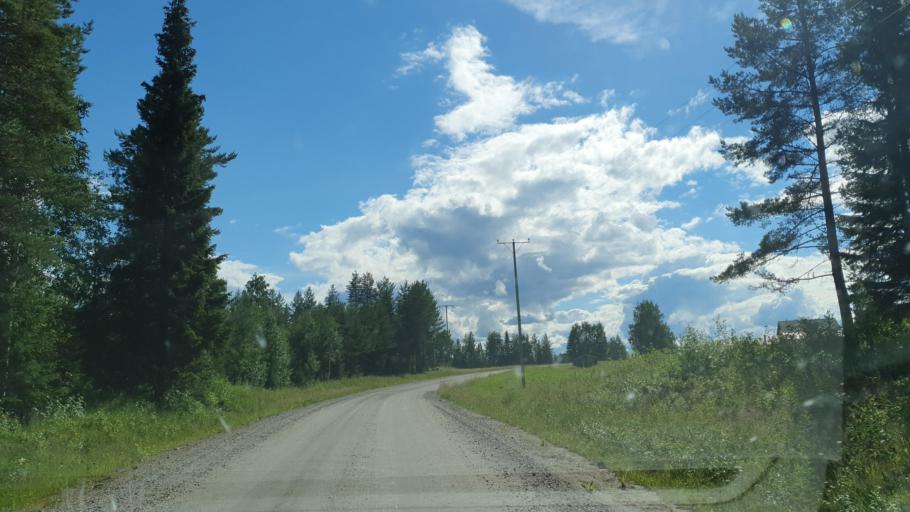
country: FI
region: Kainuu
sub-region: Kehys-Kainuu
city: Kuhmo
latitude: 64.1496
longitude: 29.7886
